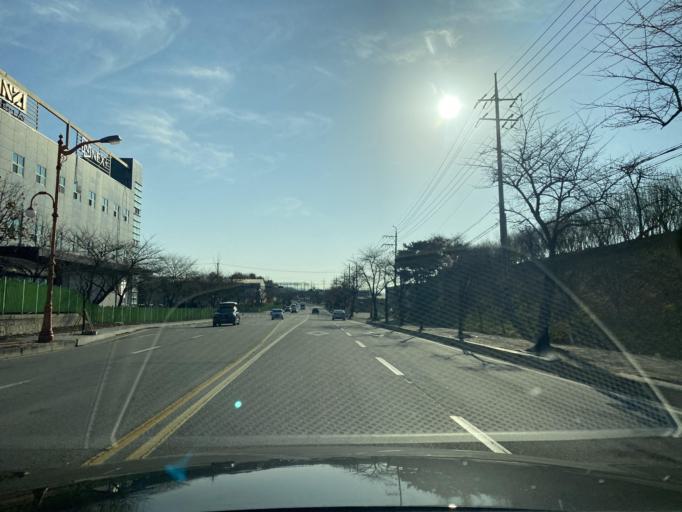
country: KR
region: Chungcheongnam-do
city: Yesan
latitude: 36.7158
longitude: 126.8431
